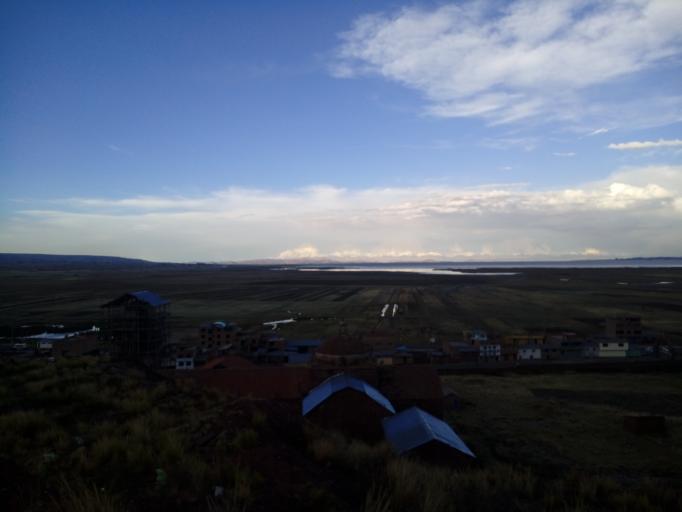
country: PE
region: Puno
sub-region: Provincia de Chucuito
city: Zepita
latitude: -16.4996
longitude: -69.1021
